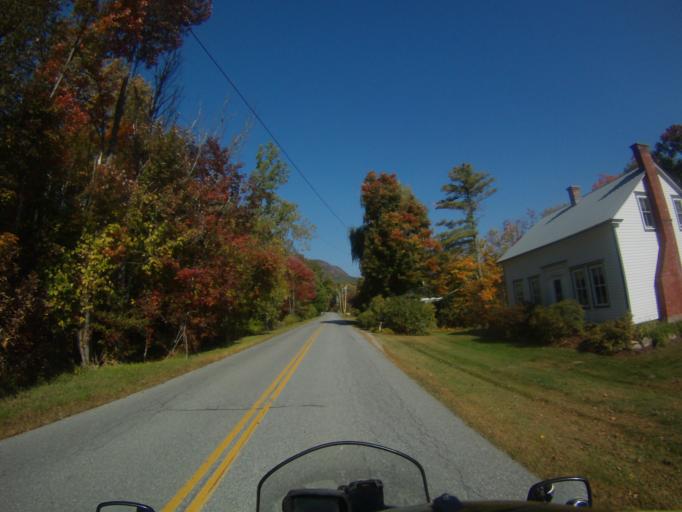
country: US
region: Vermont
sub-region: Addison County
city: Bristol
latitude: 44.1238
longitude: -73.0903
